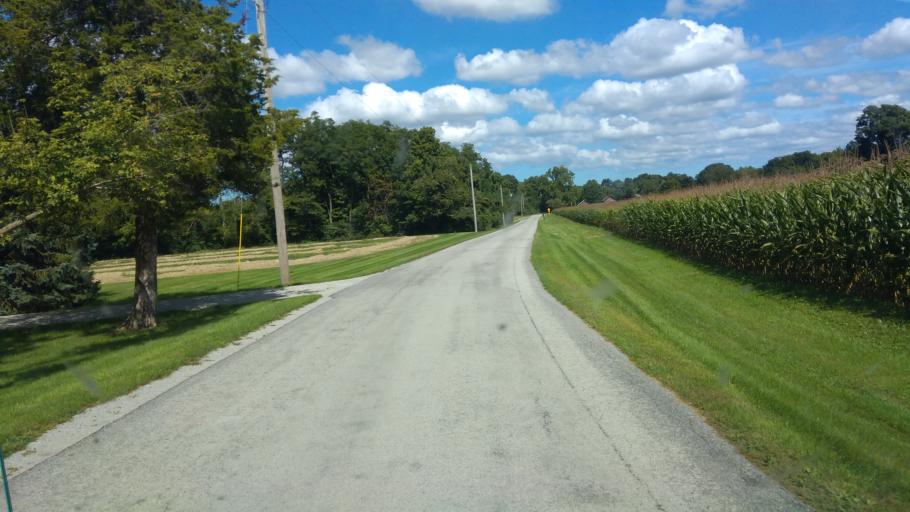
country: US
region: Ohio
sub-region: Huron County
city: Norwalk
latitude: 41.2198
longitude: -82.6547
